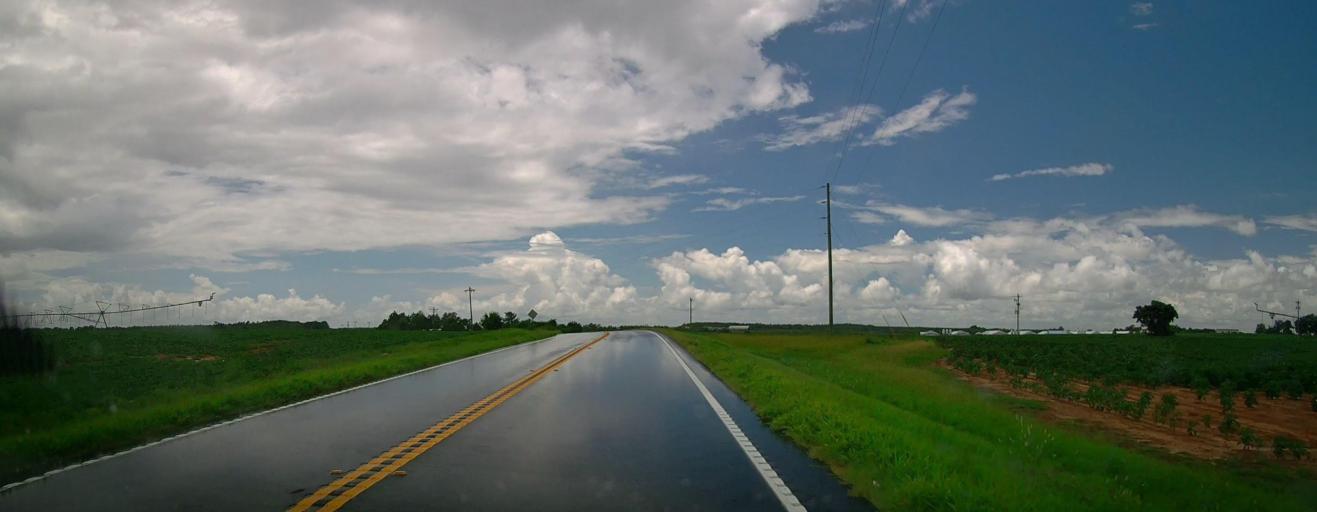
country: US
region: Georgia
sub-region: Pulaski County
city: Hawkinsville
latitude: 32.1882
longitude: -83.5241
